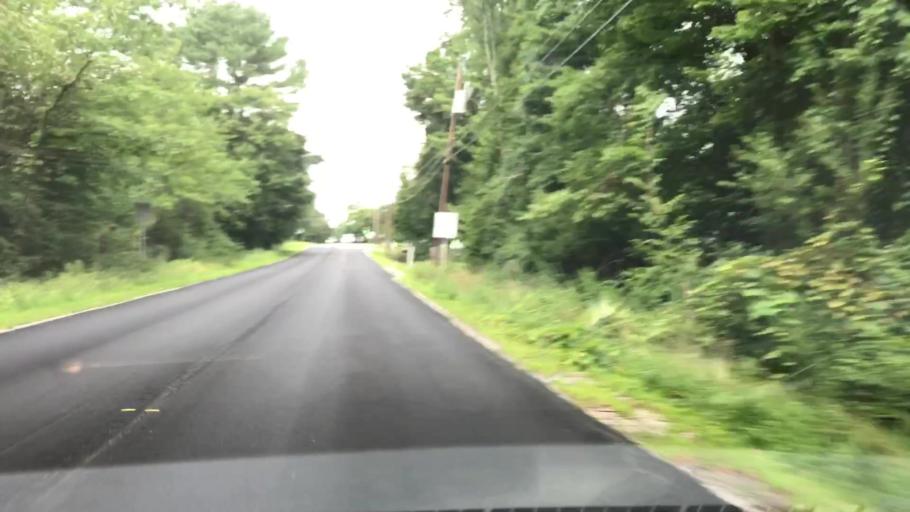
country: US
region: New Hampshire
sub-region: Hillsborough County
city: Milford
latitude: 42.8595
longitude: -71.6241
